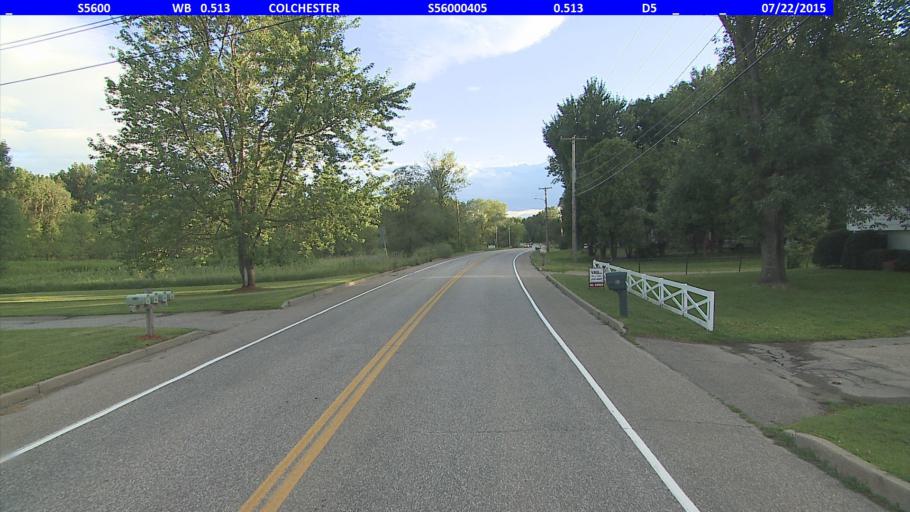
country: US
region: Vermont
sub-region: Chittenden County
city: Burlington
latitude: 44.5315
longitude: -73.2516
